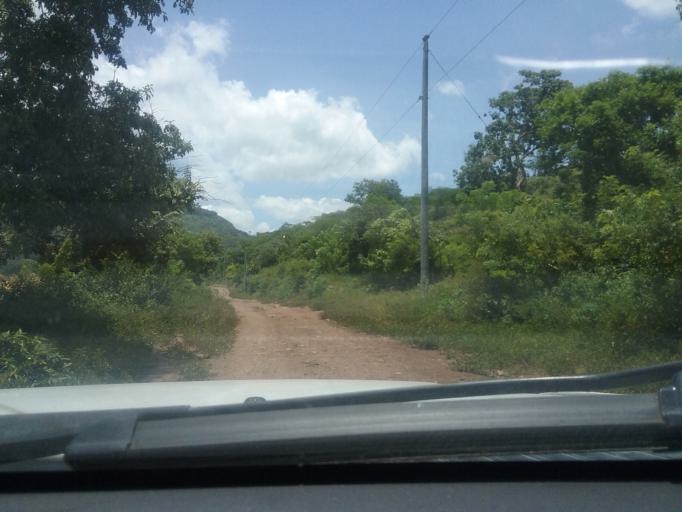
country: NI
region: Matagalpa
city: Terrabona
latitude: 12.6716
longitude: -85.9806
